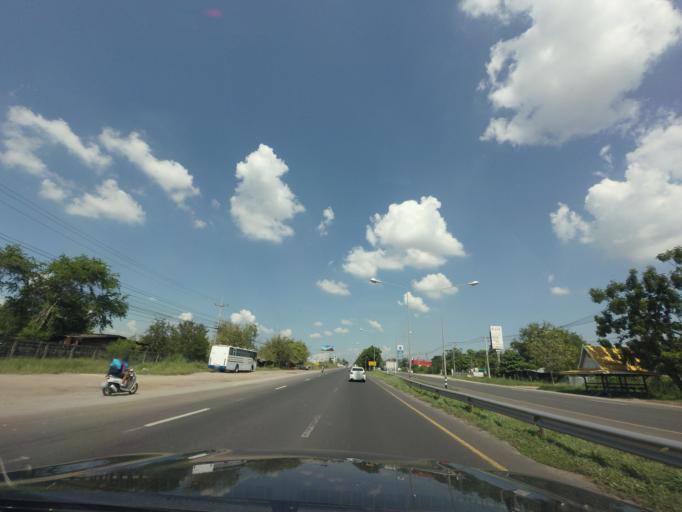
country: TH
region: Nakhon Ratchasima
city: Nakhon Ratchasima
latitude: 15.0591
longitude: 102.1686
